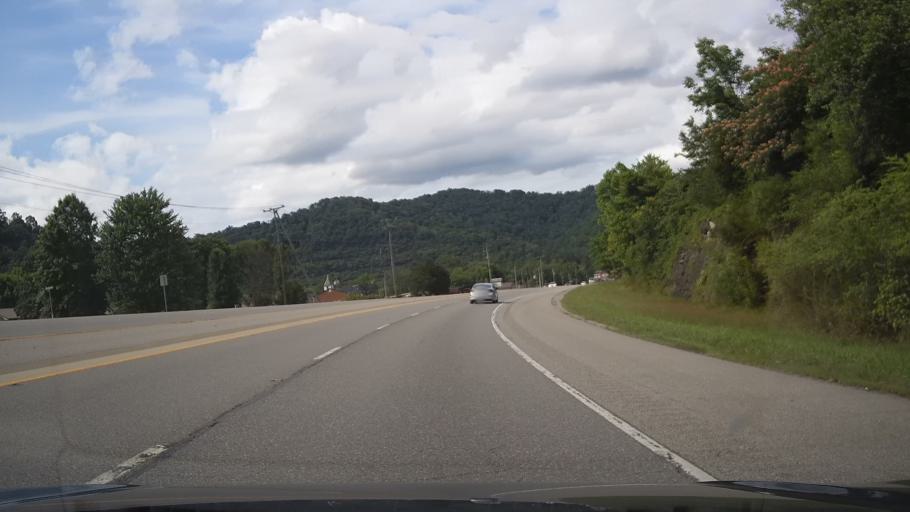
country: US
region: Kentucky
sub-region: Pike County
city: Coal Run Village
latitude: 37.5476
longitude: -82.6335
